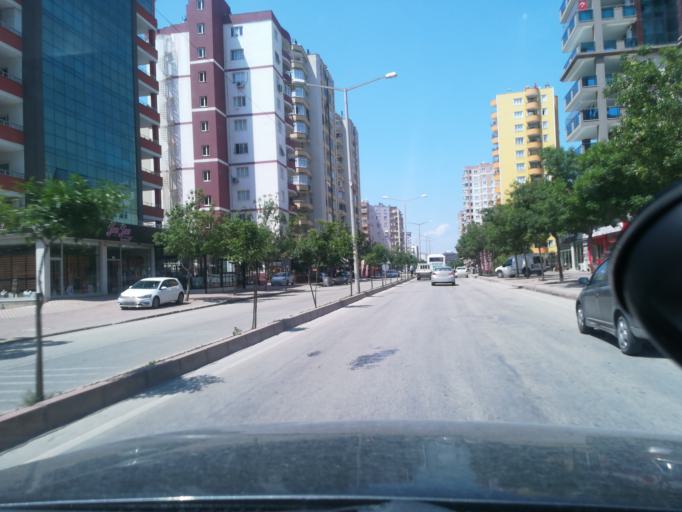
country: TR
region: Adana
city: Seyhan
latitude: 37.0346
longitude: 35.2630
